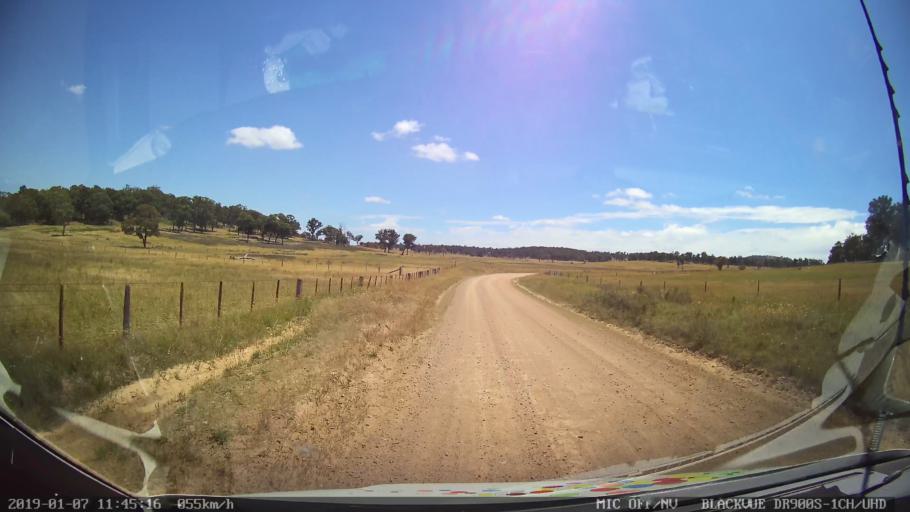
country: AU
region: New South Wales
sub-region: Guyra
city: Guyra
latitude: -30.3471
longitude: 151.6051
